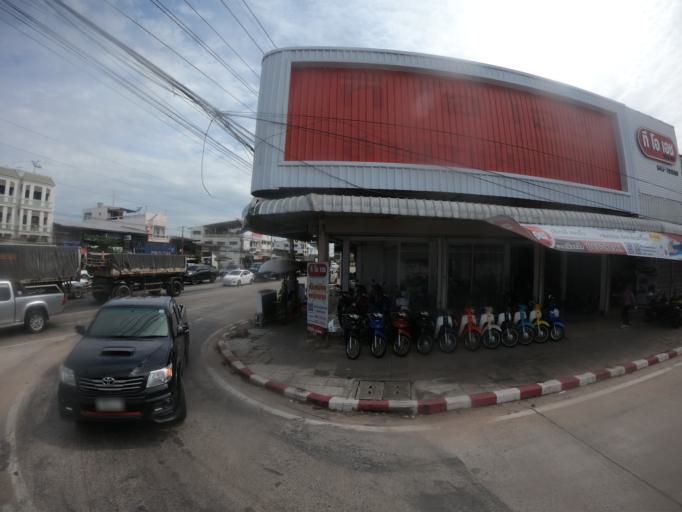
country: TH
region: Maha Sarakham
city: Chiang Yuen
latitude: 16.4098
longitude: 103.0981
